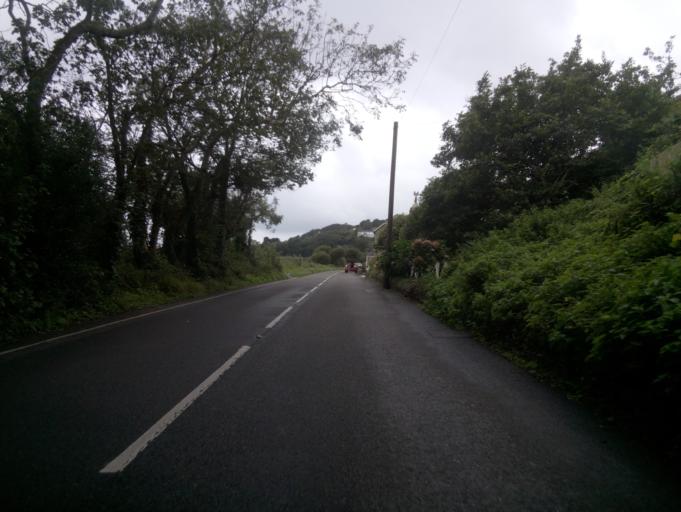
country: GB
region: England
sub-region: Devon
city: Dartmouth
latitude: 50.2702
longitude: -3.6566
